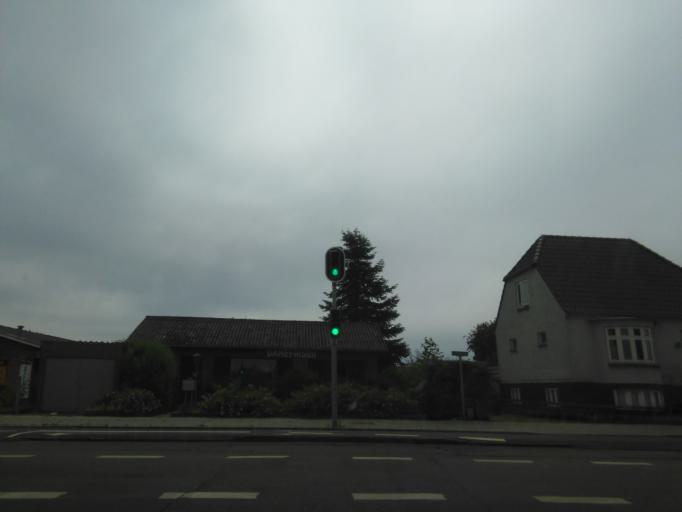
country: DK
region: Central Jutland
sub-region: Horsens Kommune
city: Horsens
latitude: 55.8681
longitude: 9.8866
